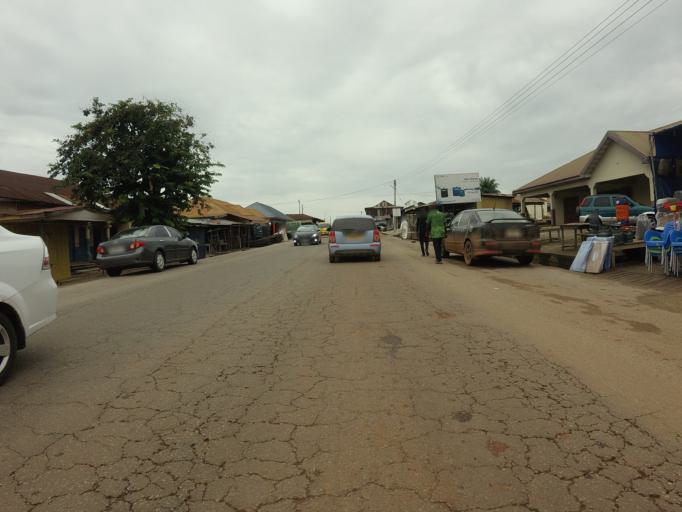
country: GH
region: Eastern
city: Begoro
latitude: 6.3787
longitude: -0.5472
